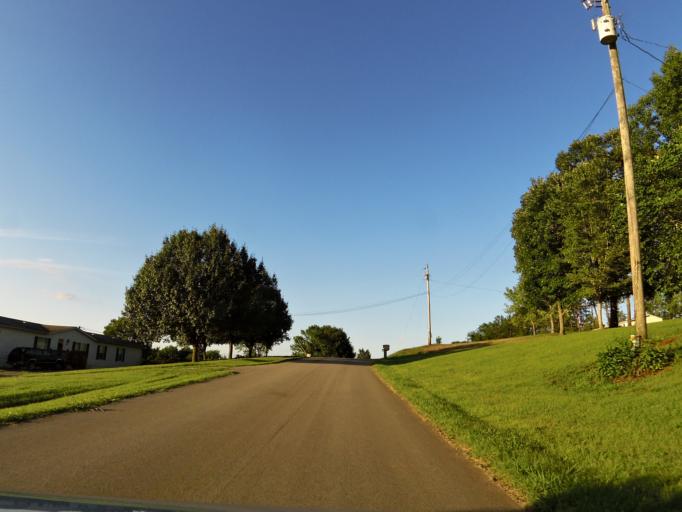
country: US
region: Tennessee
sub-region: Loudon County
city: Greenback
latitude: 35.7107
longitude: -84.2179
